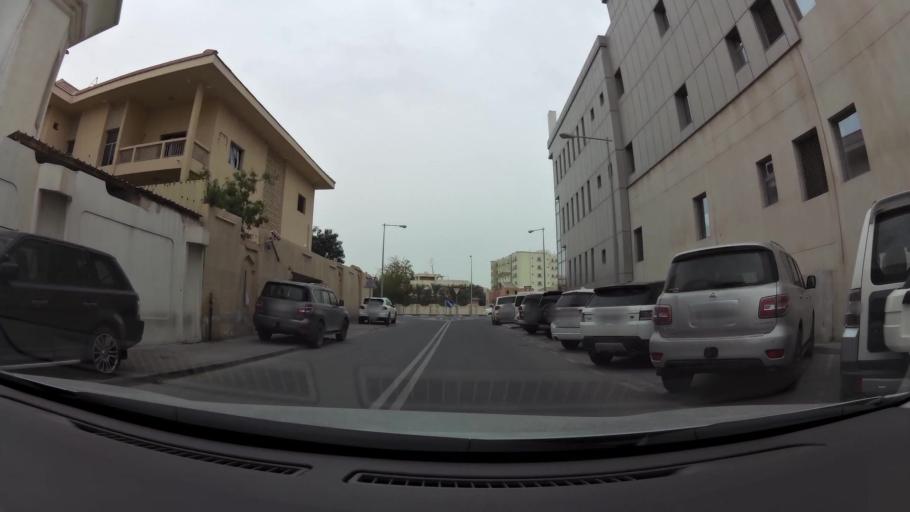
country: QA
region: Baladiyat ad Dawhah
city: Doha
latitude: 25.2638
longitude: 51.5198
